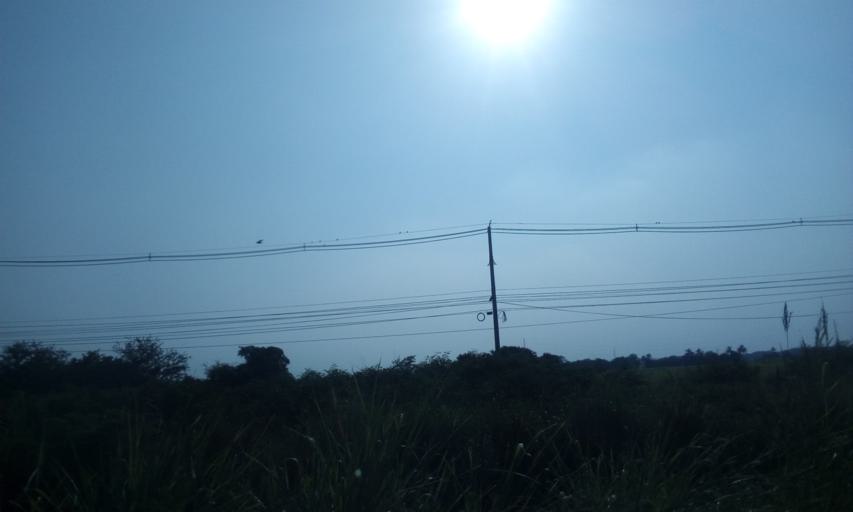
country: TH
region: Sing Buri
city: Phrom Buri
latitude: 14.8166
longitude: 100.4330
